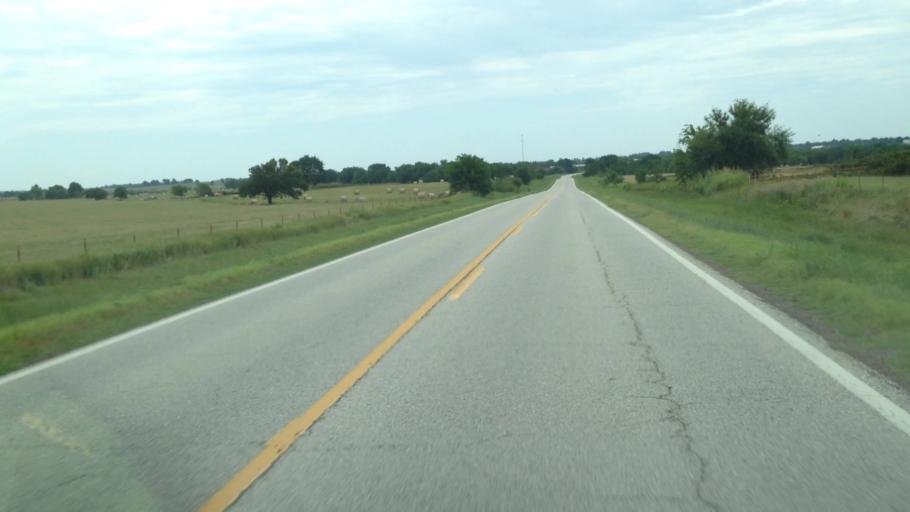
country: US
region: Kansas
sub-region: Labette County
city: Chetopa
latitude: 36.8554
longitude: -95.1173
